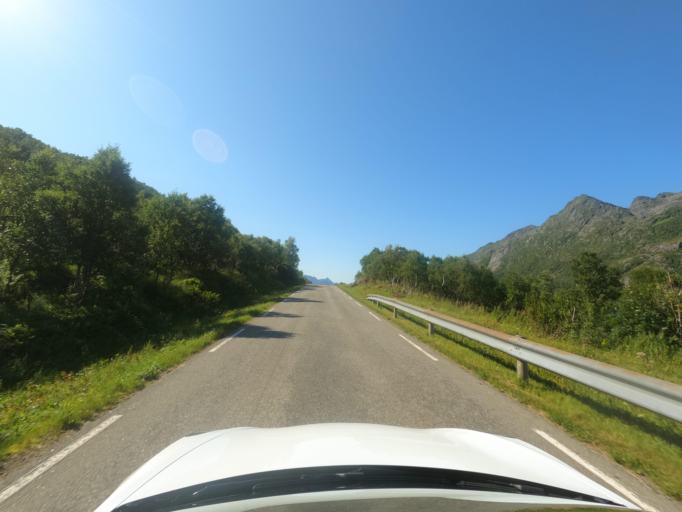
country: NO
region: Nordland
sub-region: Hadsel
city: Stokmarknes
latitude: 68.3871
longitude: 15.0948
